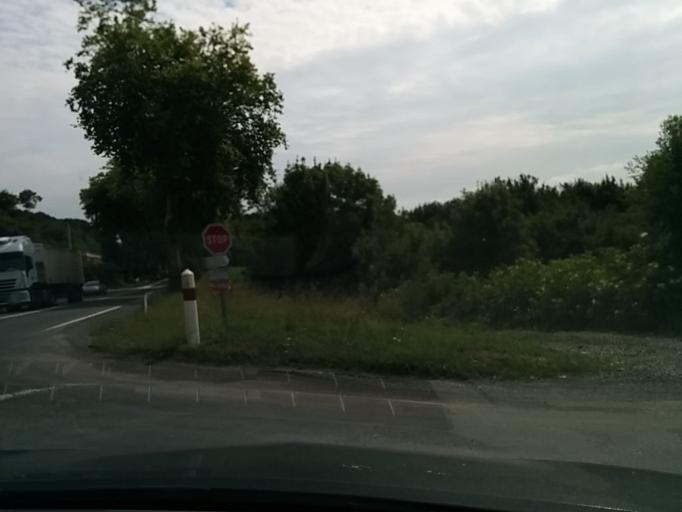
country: FR
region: Aquitaine
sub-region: Departement des Pyrenees-Atlantiques
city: Urrugne
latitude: 43.3601
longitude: -1.7253
